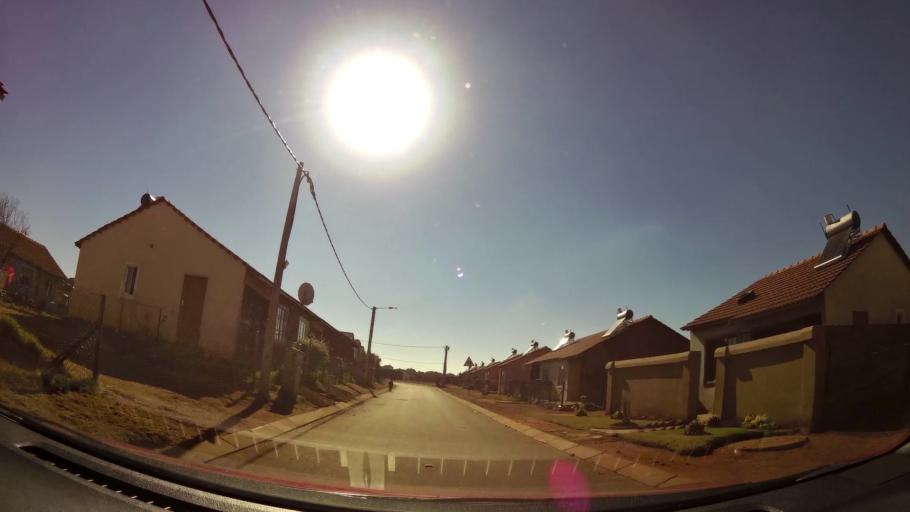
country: ZA
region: Gauteng
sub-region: City of Johannesburg Metropolitan Municipality
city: Soweto
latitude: -26.2381
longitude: 27.7993
